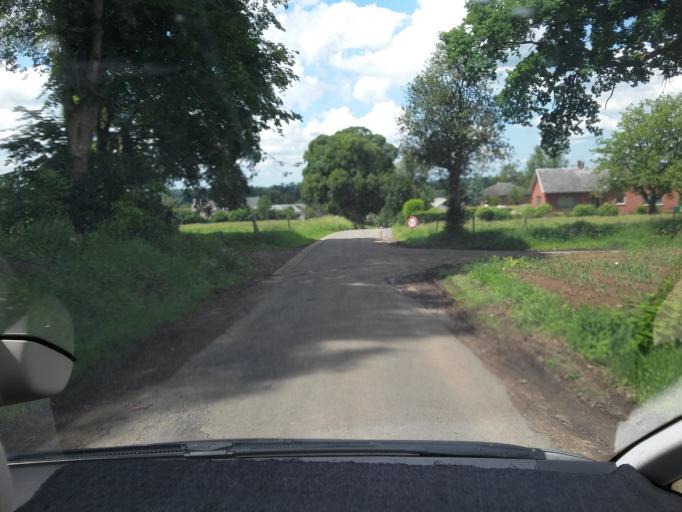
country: BE
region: Wallonia
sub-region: Province de Namur
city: Hamois
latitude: 50.3134
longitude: 5.1543
